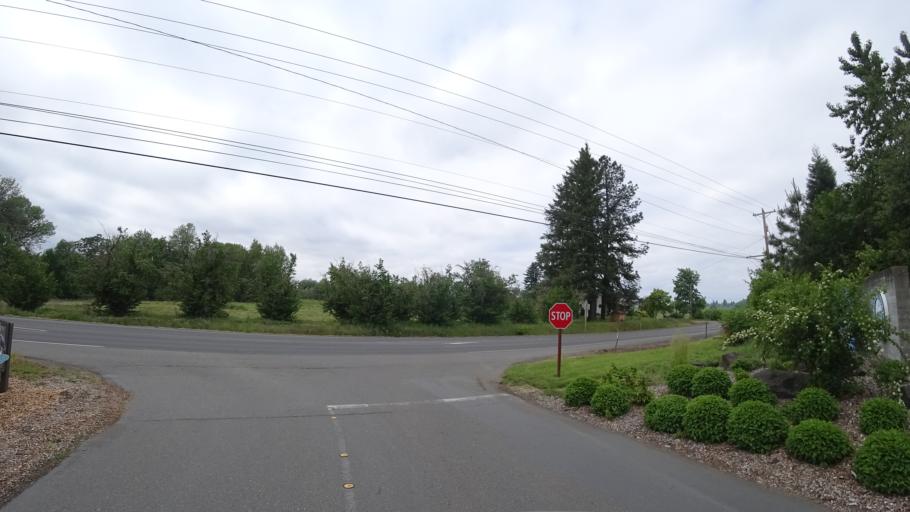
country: US
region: Oregon
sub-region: Washington County
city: Hillsboro
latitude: 45.5010
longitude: -122.9908
